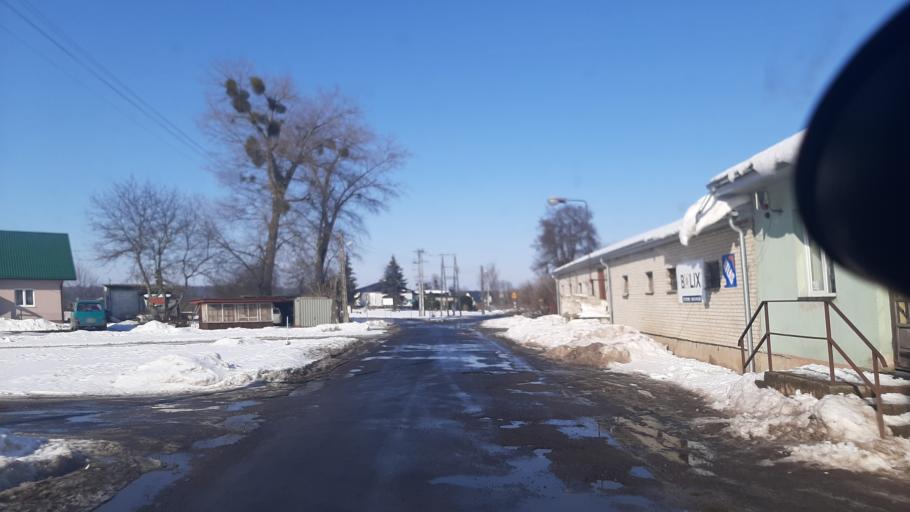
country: PL
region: Lublin Voivodeship
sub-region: Powiat lubelski
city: Wojciechow
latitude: 51.2876
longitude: 22.2809
